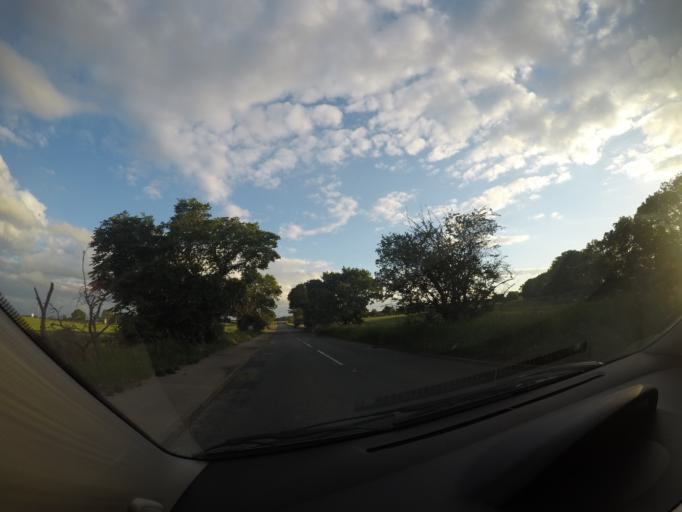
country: GB
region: England
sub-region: North Yorkshire
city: Catterick
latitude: 54.3840
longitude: -1.6573
